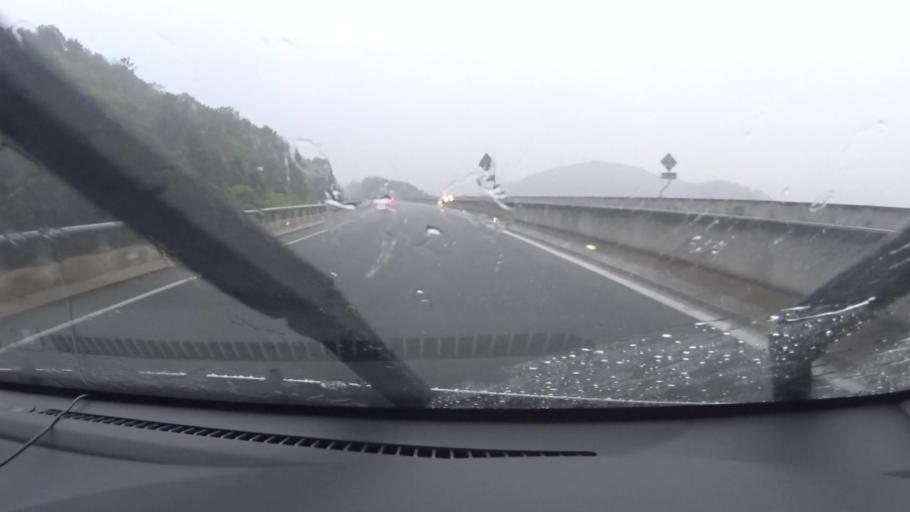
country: JP
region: Kyoto
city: Kameoka
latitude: 35.1159
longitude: 135.4800
